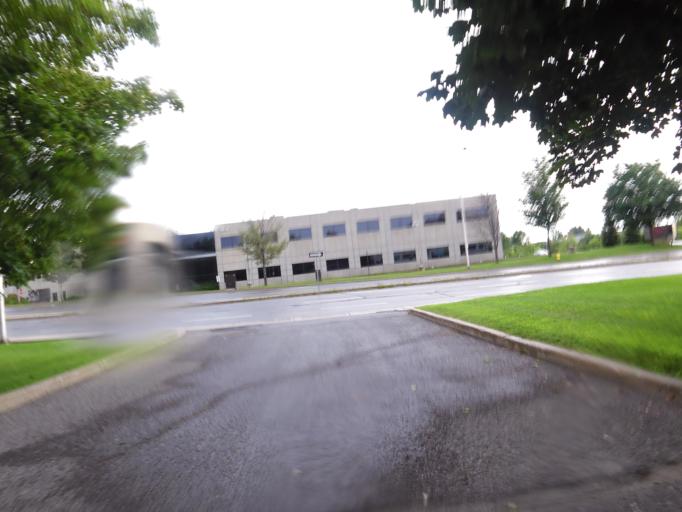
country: CA
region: Ontario
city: Bells Corners
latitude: 45.3002
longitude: -75.9093
